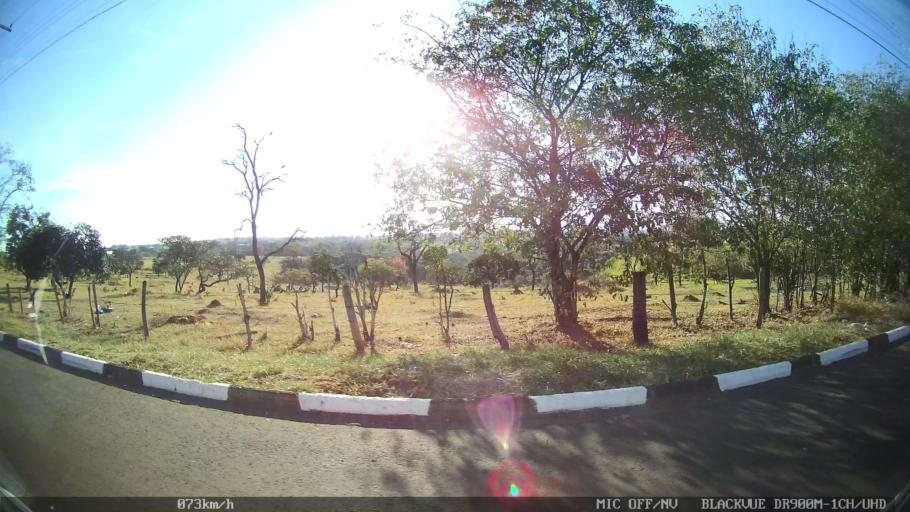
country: BR
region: Sao Paulo
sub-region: Franca
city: Franca
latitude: -20.5111
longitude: -47.3750
